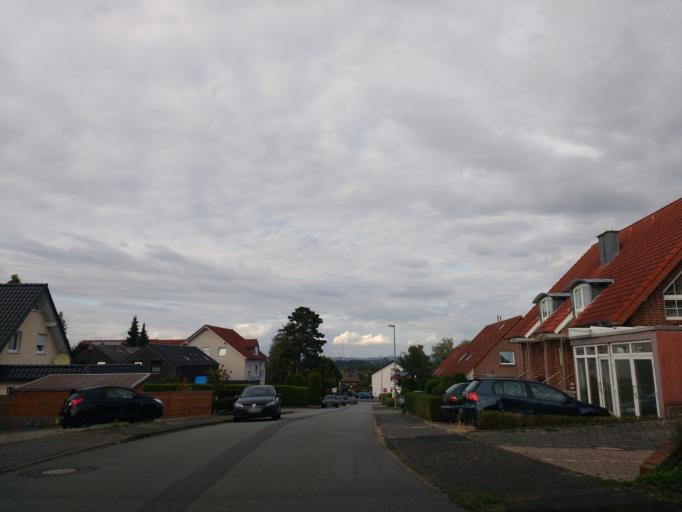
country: DE
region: North Rhine-Westphalia
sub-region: Regierungsbezirk Detmold
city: Lage
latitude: 51.9394
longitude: 8.8034
